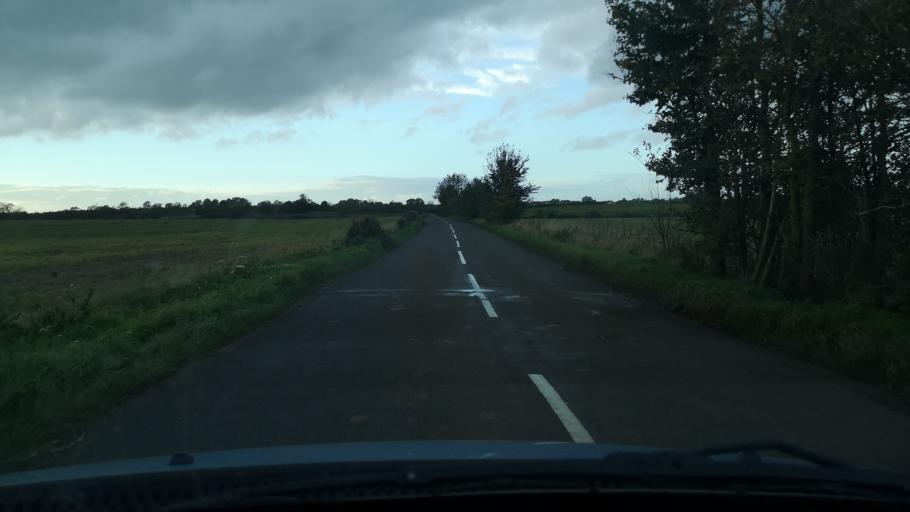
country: GB
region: England
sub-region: Doncaster
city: Norton
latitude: 53.6355
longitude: -1.2042
